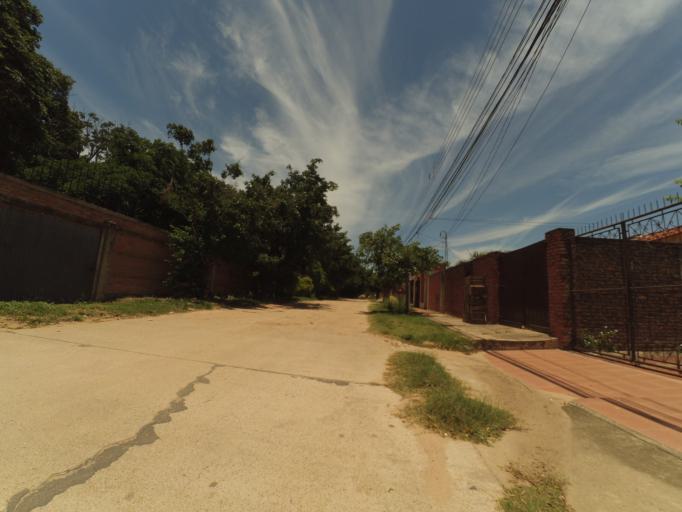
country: BO
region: Santa Cruz
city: Santa Cruz de la Sierra
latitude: -17.8108
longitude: -63.2295
